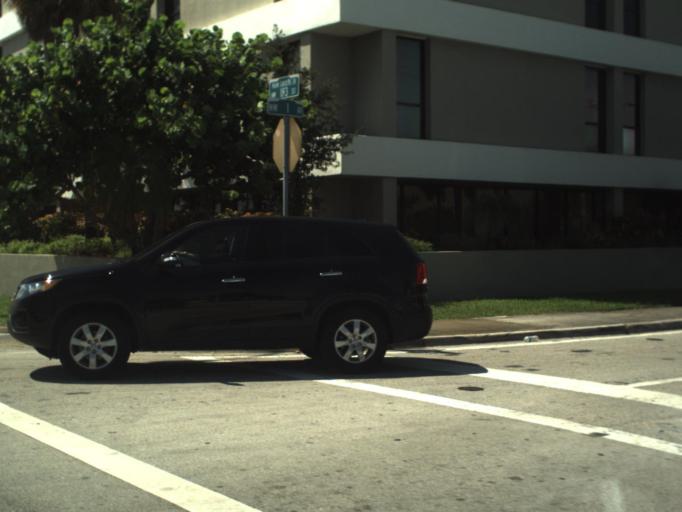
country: US
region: Florida
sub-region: Miami-Dade County
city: Norland
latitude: 25.9427
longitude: -80.2031
